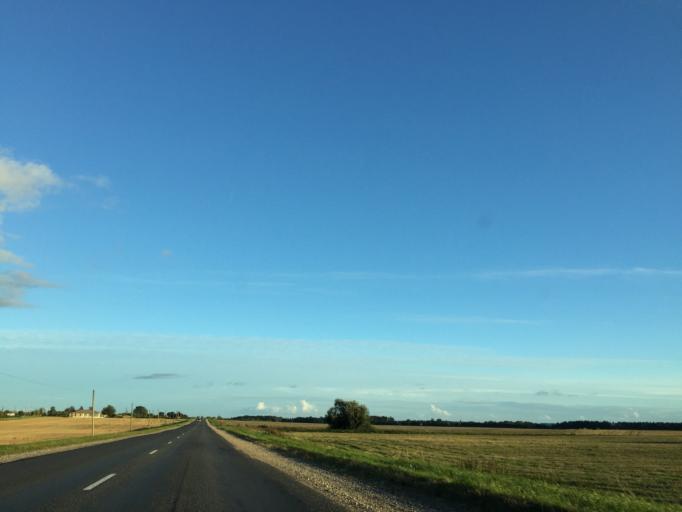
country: LV
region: Saldus Rajons
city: Saldus
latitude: 56.7020
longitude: 22.4296
